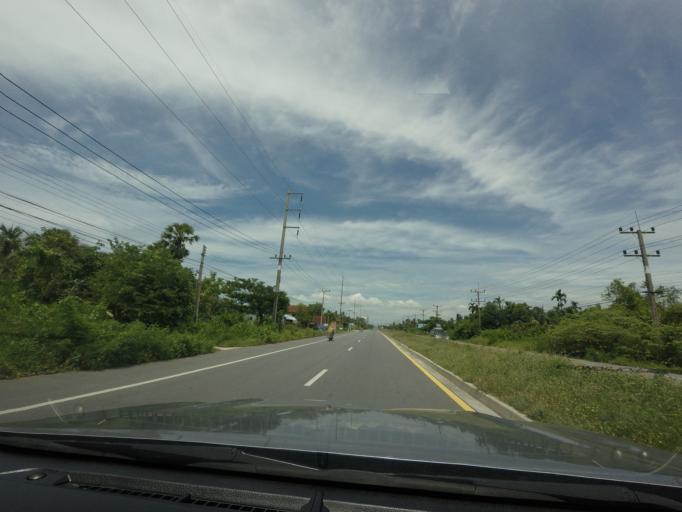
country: TH
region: Songkhla
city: Ranot
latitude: 7.7320
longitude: 100.3667
